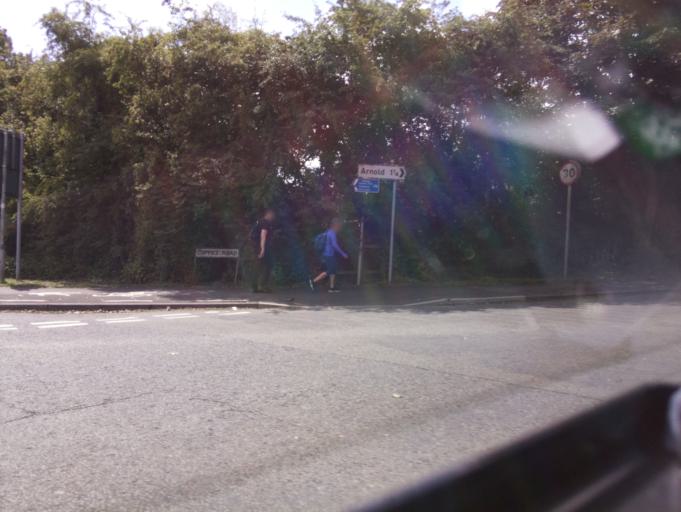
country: GB
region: England
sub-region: Nottinghamshire
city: Arnold
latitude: 53.0012
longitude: -1.1015
